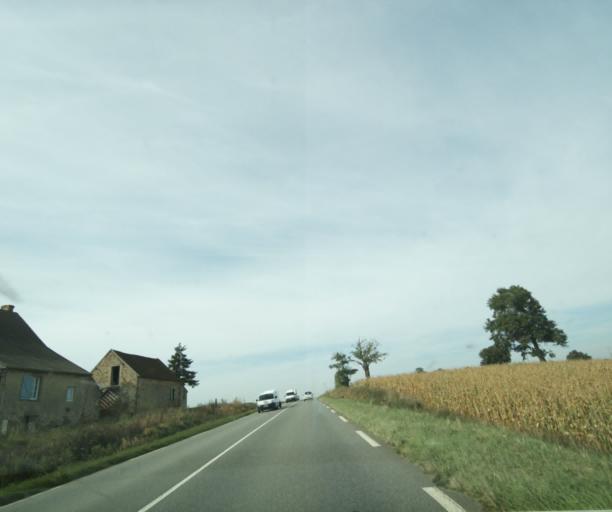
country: FR
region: Auvergne
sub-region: Departement de l'Allier
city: Le Donjon
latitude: 46.3679
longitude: 3.8529
